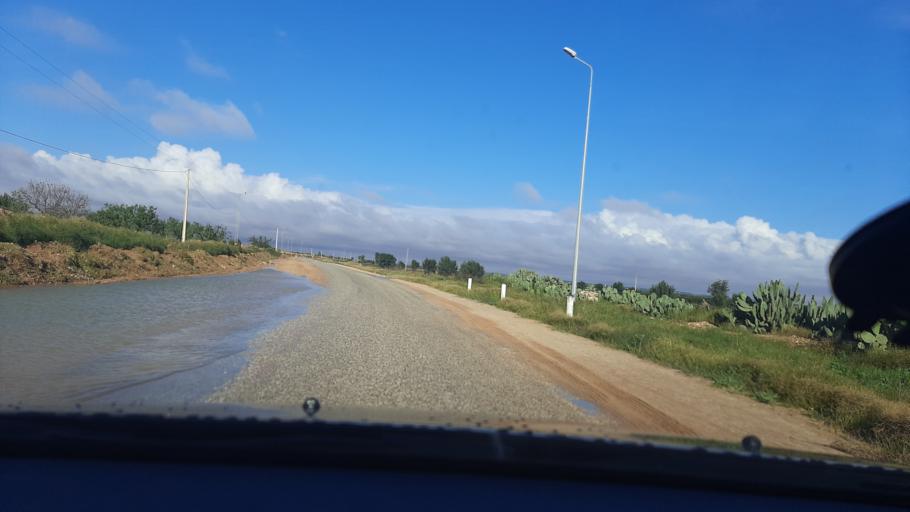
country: TN
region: Safaqis
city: Sfax
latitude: 34.8866
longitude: 10.6259
